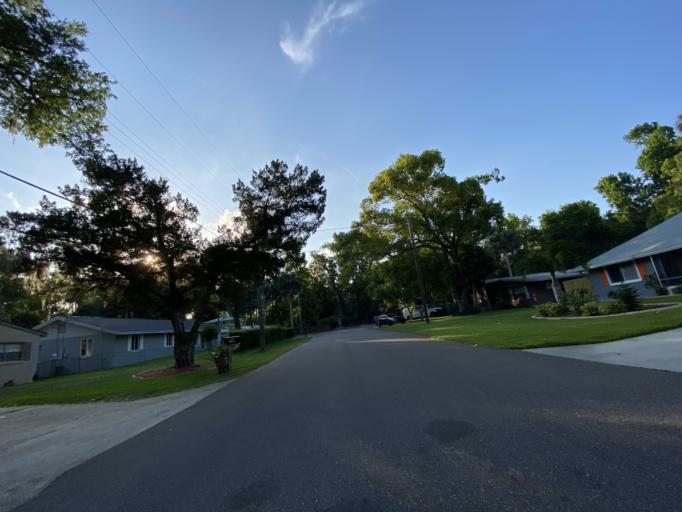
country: US
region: Florida
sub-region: Volusia County
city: Port Orange
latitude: 29.1443
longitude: -81.0049
